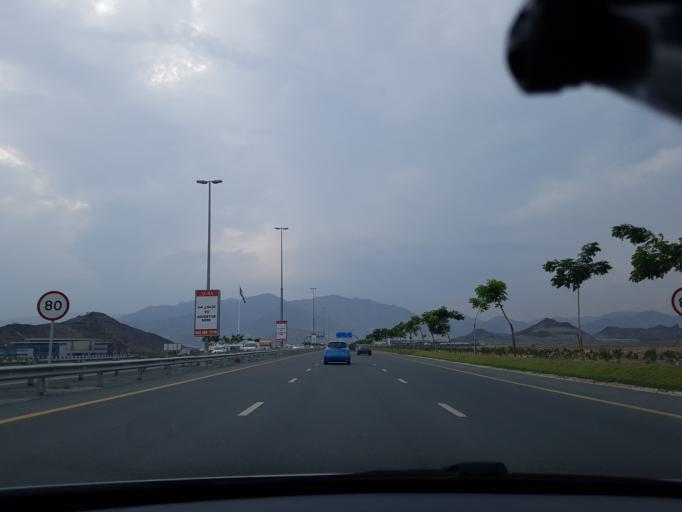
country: AE
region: Al Fujayrah
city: Al Fujayrah
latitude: 25.1226
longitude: 56.2931
